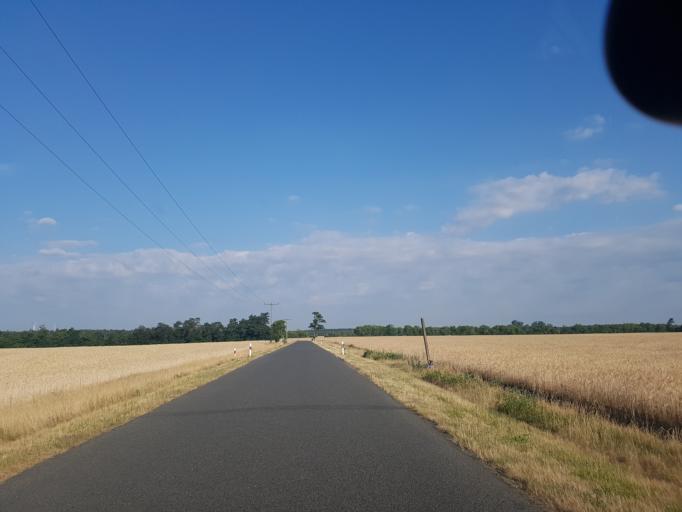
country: DE
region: Saxony-Anhalt
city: Seyda
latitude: 51.9224
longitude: 12.9338
